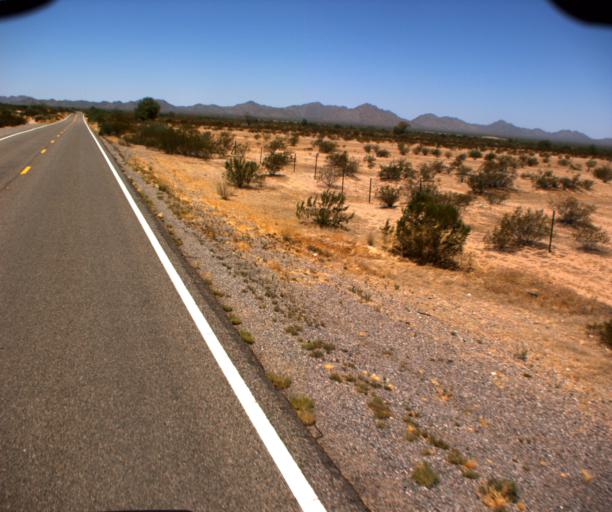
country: US
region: Arizona
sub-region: Pinal County
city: Maricopa
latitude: 33.0346
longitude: -112.3530
